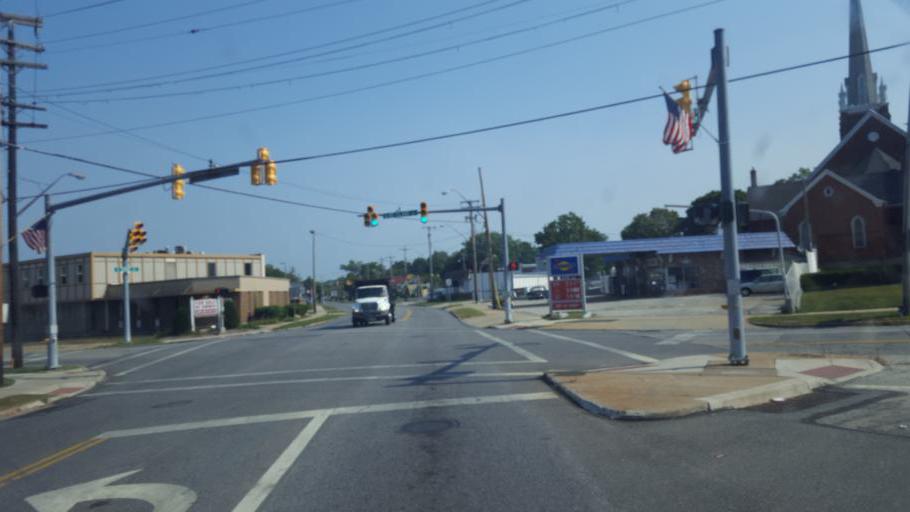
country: US
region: Ohio
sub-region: Lake County
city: Painesville
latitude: 41.7277
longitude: -81.2444
